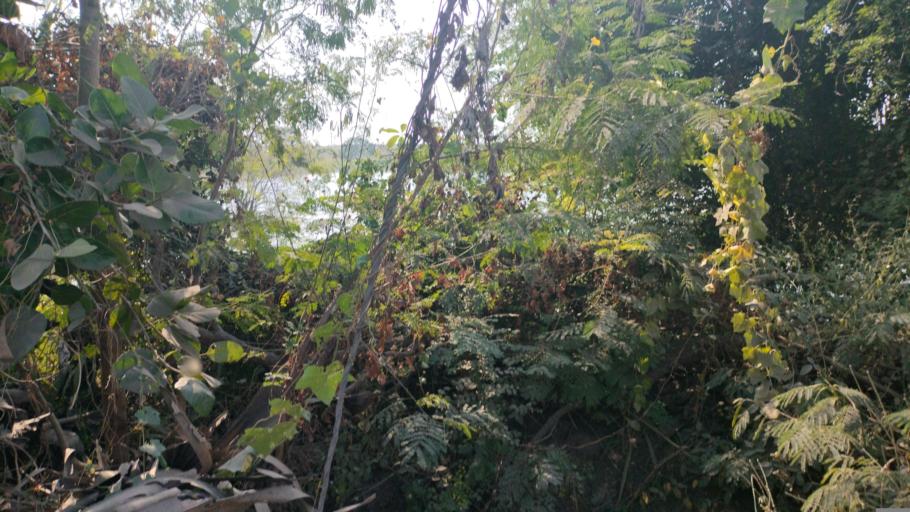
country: IN
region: Maharashtra
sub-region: Thane
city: Virar
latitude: 19.5147
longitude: 72.8513
